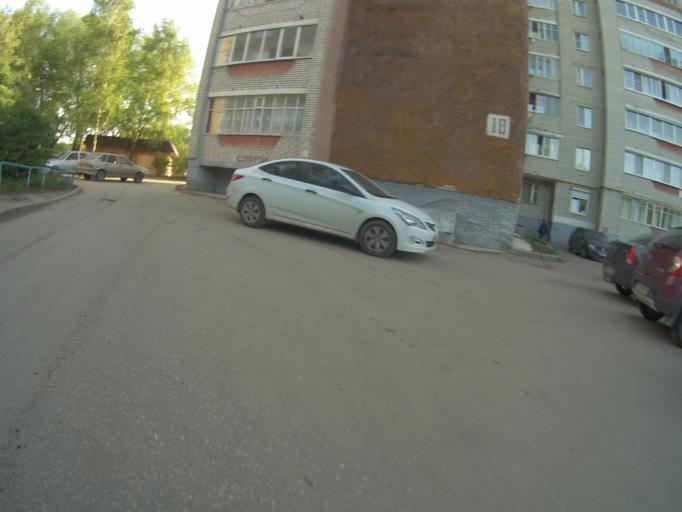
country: RU
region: Vladimir
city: Kommunar
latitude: 56.1685
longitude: 40.4560
